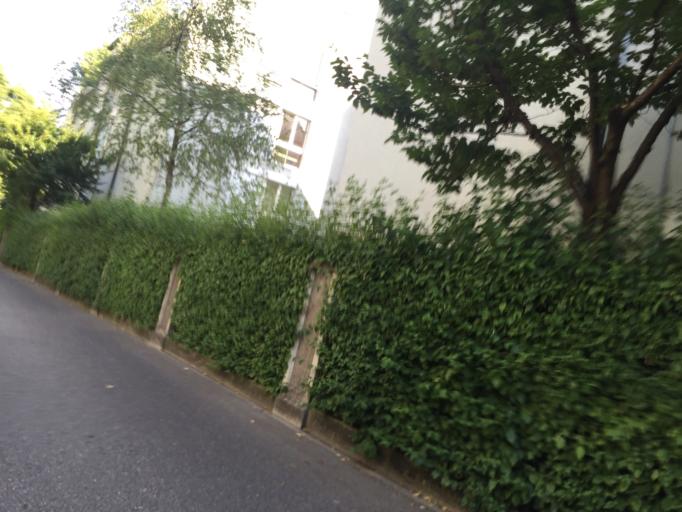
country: CH
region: Bern
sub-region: Bern-Mittelland District
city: Bern
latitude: 46.9429
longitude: 7.4335
